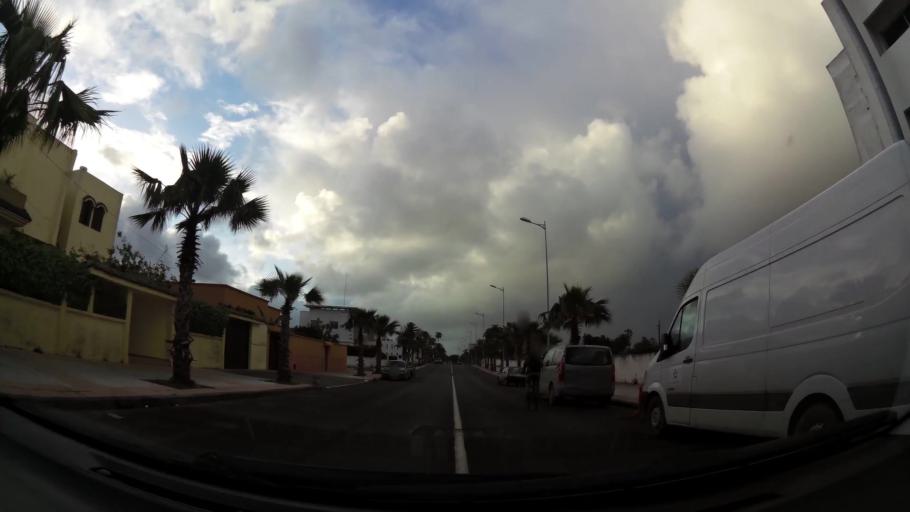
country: MA
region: Doukkala-Abda
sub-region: El-Jadida
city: El Jadida
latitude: 33.2428
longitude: -8.5043
